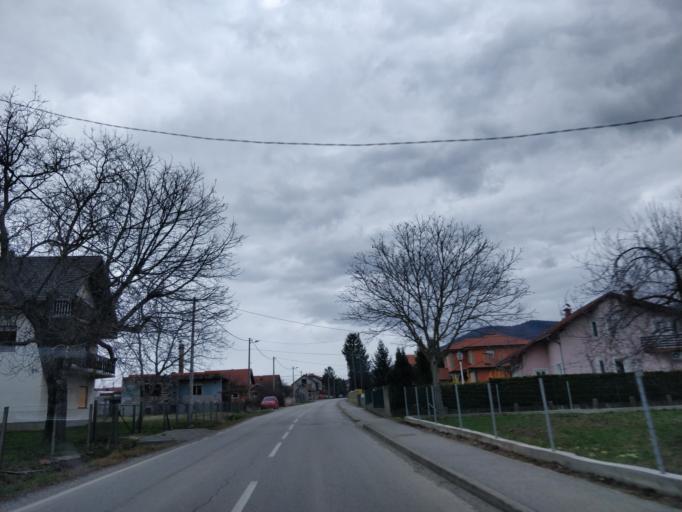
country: HR
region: Zagrebacka
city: Jablanovec
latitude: 45.9080
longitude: 15.8777
